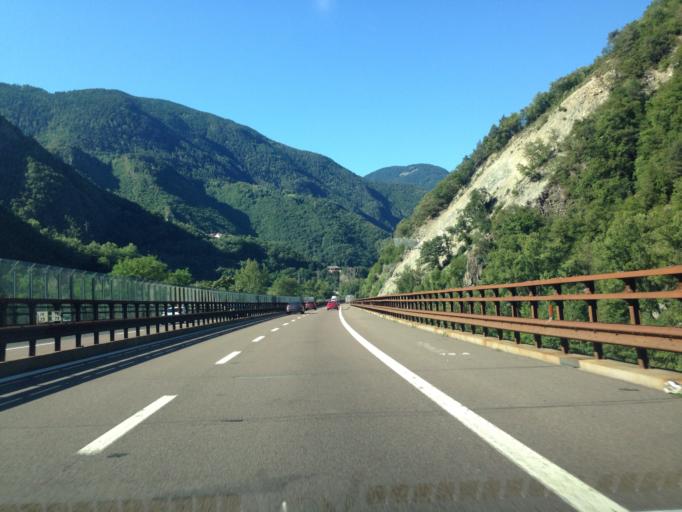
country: IT
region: Trentino-Alto Adige
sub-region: Bolzano
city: Collalbo
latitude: 46.5009
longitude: 11.4532
